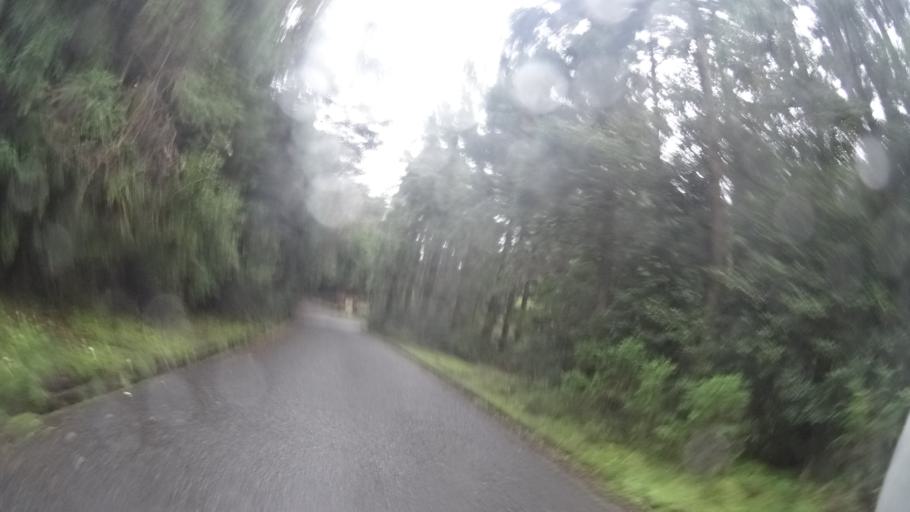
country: JP
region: Kagoshima
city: Nishinoomote
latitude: 30.3022
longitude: 130.5795
